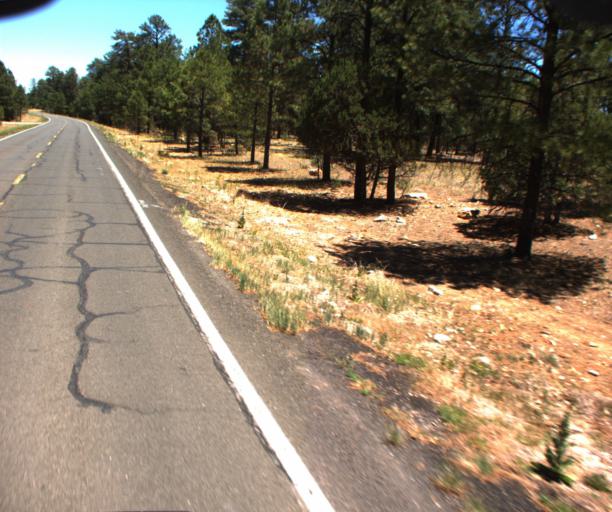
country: US
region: Arizona
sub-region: Gila County
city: Star Valley
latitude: 34.6269
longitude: -111.1331
